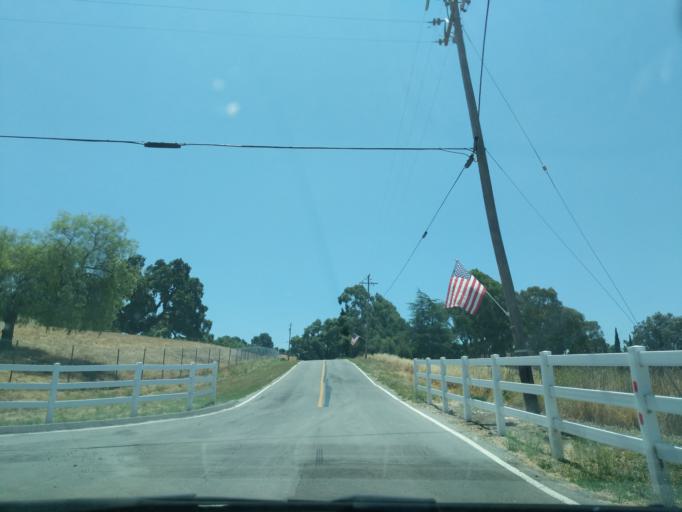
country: US
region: California
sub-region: Santa Clara County
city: San Martin
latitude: 37.1187
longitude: -121.5843
